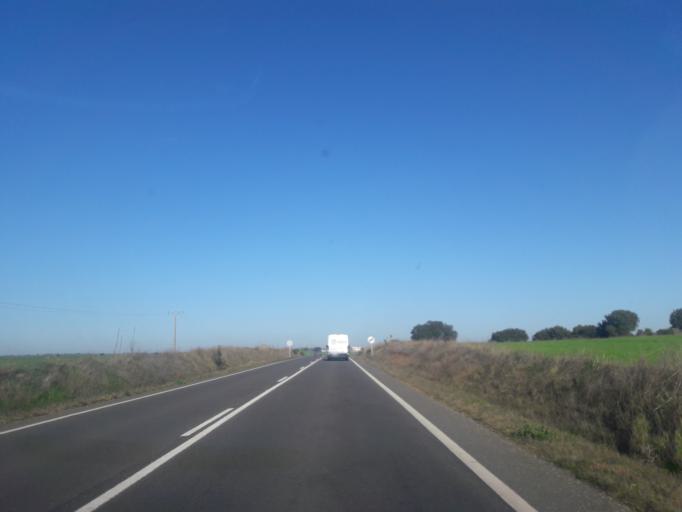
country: ES
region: Castille and Leon
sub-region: Provincia de Salamanca
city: Villarmayor
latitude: 41.0085
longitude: -5.9538
